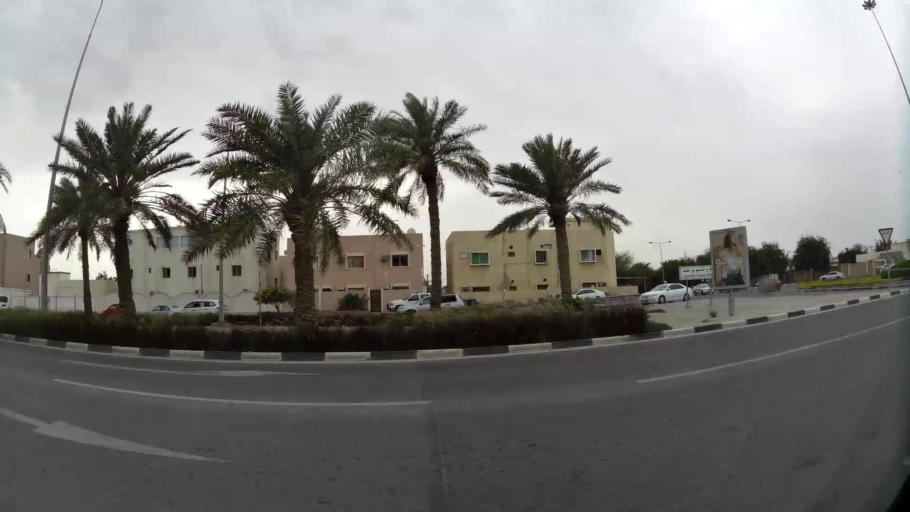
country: QA
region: Baladiyat ad Dawhah
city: Doha
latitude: 25.3144
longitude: 51.4872
